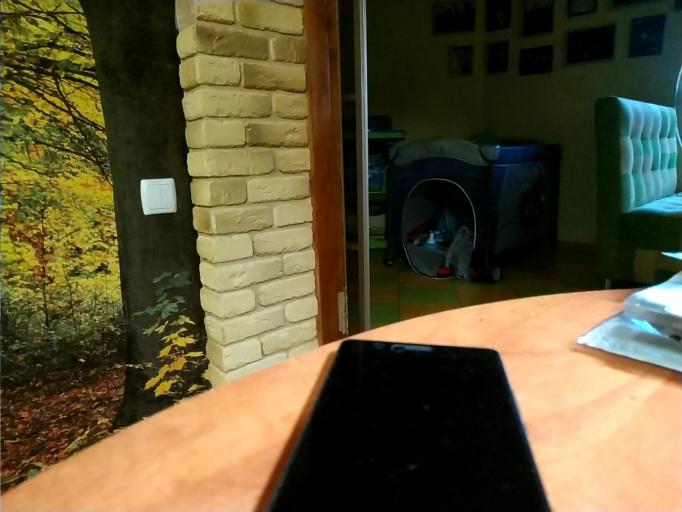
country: RU
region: Orjol
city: Znamenskoye
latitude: 53.4451
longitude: 35.5282
